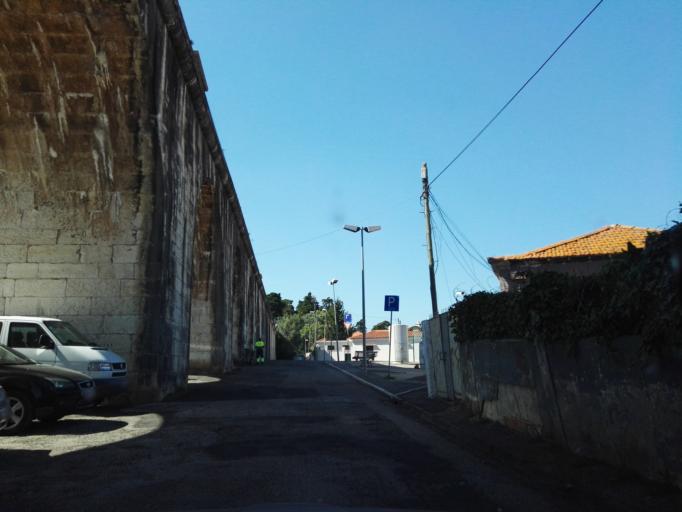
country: PT
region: Lisbon
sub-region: Lisbon
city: Lisbon
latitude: 38.7321
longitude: -9.1718
